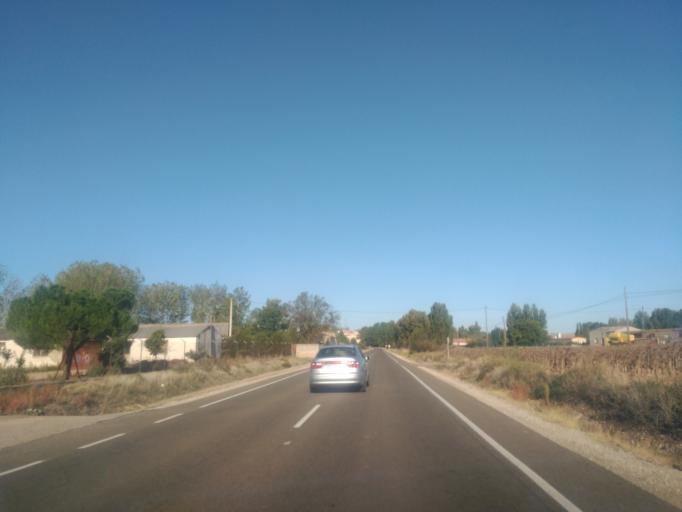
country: ES
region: Castille and Leon
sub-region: Provincia de Burgos
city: Quemada
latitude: 41.6974
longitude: -3.5649
